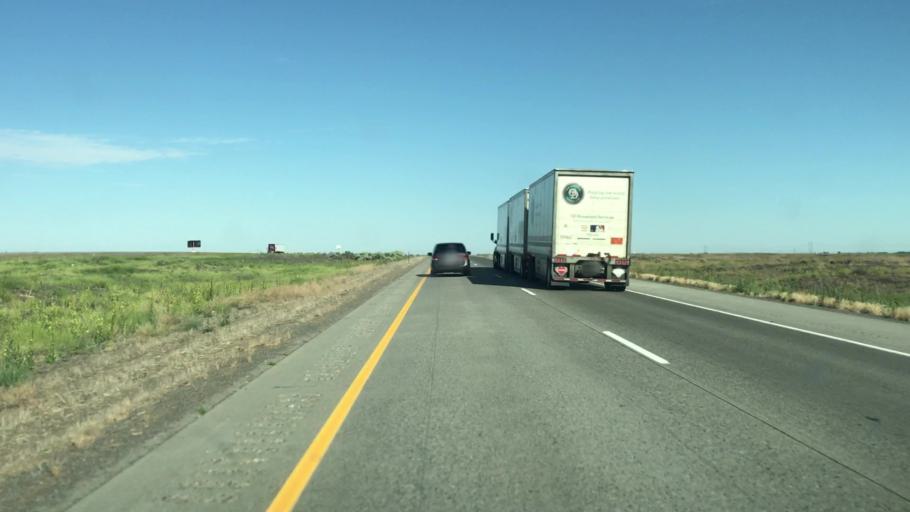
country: US
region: Idaho
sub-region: Twin Falls County
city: Twin Falls
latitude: 42.6249
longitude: -114.3963
